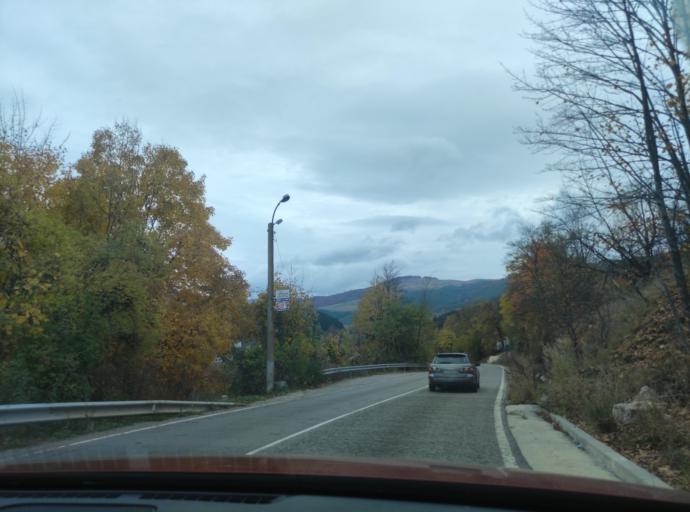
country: BG
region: Sofiya
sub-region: Obshtina Godech
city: Godech
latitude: 43.0661
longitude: 23.1076
